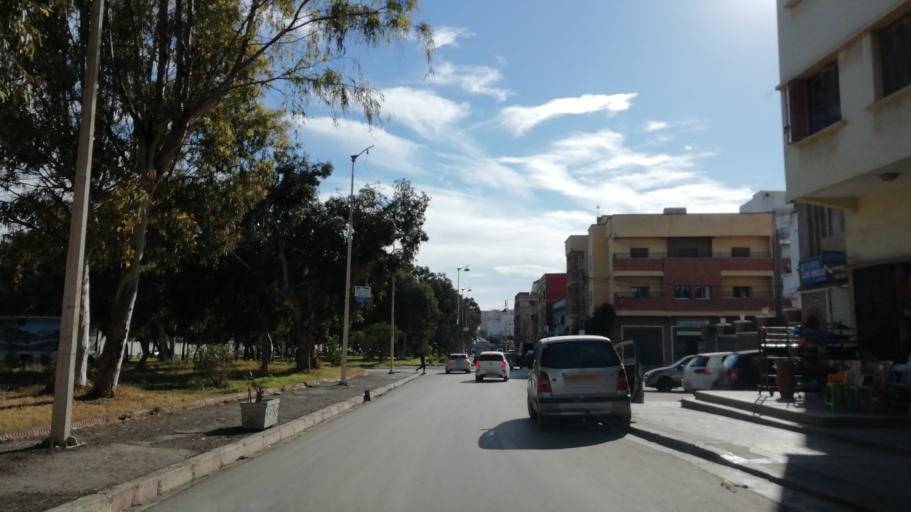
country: DZ
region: Oran
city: Oran
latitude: 35.6966
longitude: -0.6194
